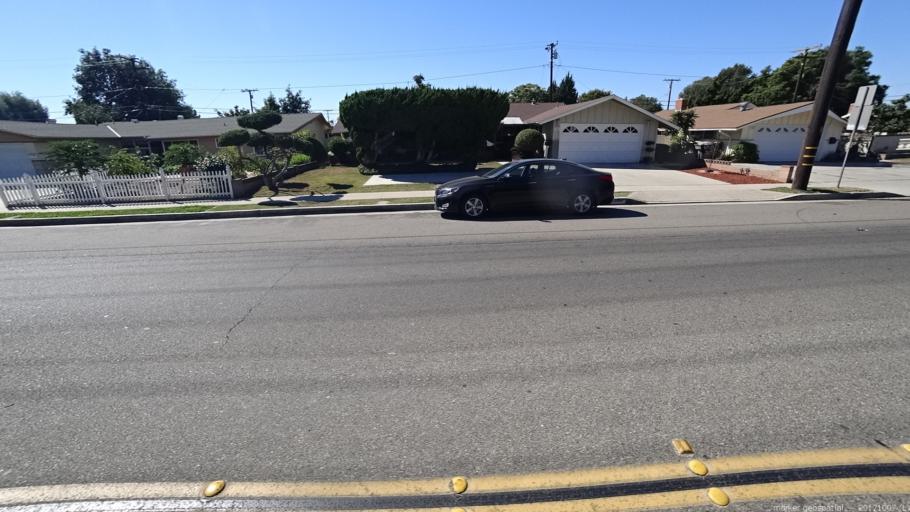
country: US
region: California
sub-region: Orange County
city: Stanton
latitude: 33.7803
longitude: -117.9840
